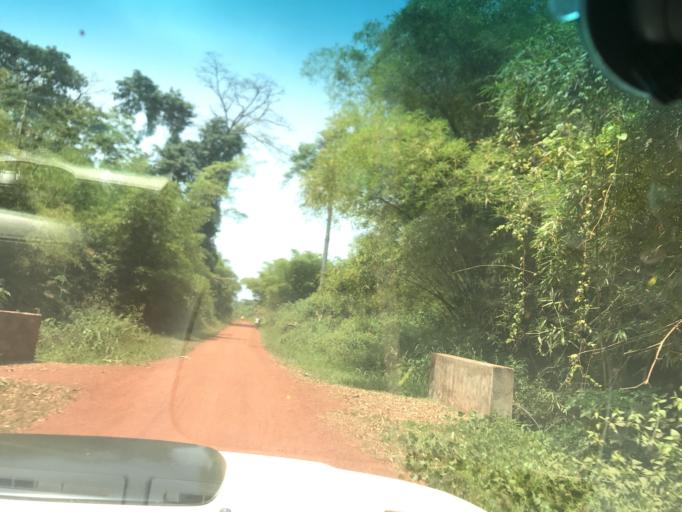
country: CD
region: Eastern Province
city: Aketi
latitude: 2.8497
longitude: 23.9193
